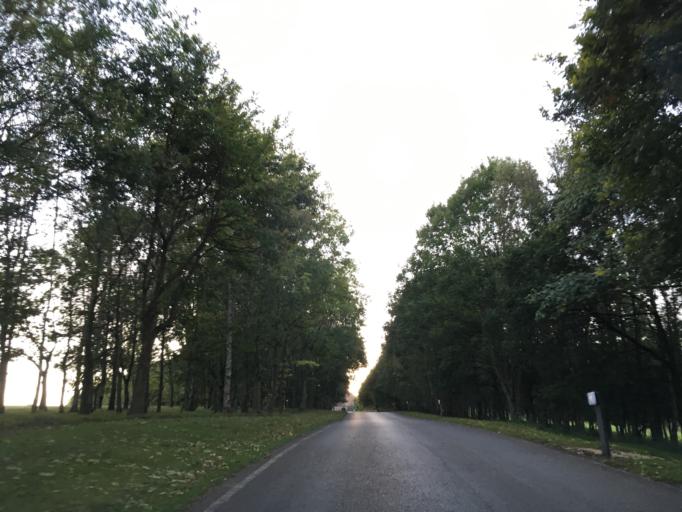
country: GB
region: England
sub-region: South Gloucestershire
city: Alveston
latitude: 51.6008
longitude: -2.5329
